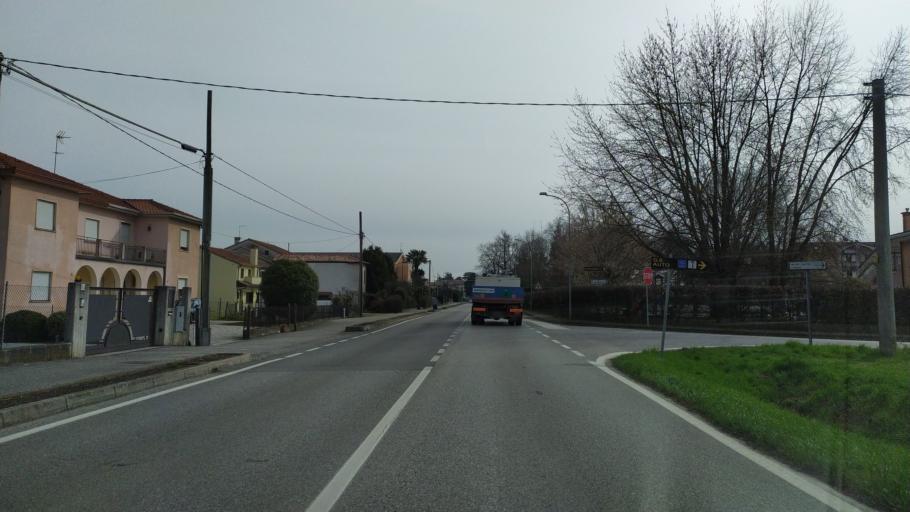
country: IT
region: Veneto
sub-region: Provincia di Padova
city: Villa del Conte
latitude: 45.5845
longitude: 11.8532
